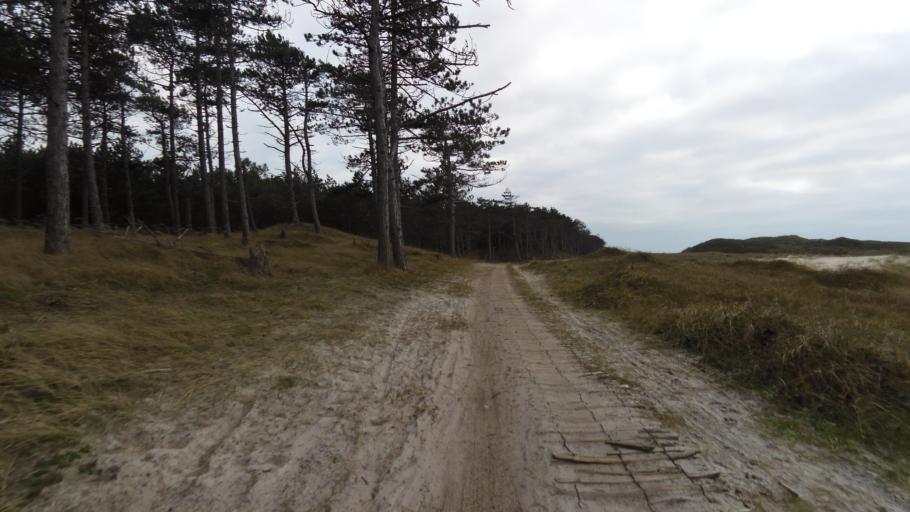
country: NL
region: North Holland
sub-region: Gemeente Bergen
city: Egmond aan Zee
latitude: 52.6893
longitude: 4.6434
